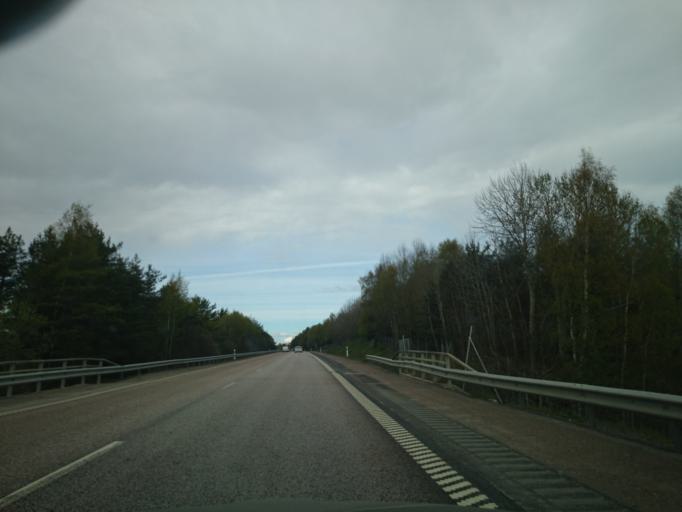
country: SE
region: Stockholm
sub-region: Sigtuna Kommun
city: Marsta
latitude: 59.6472
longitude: 17.8917
